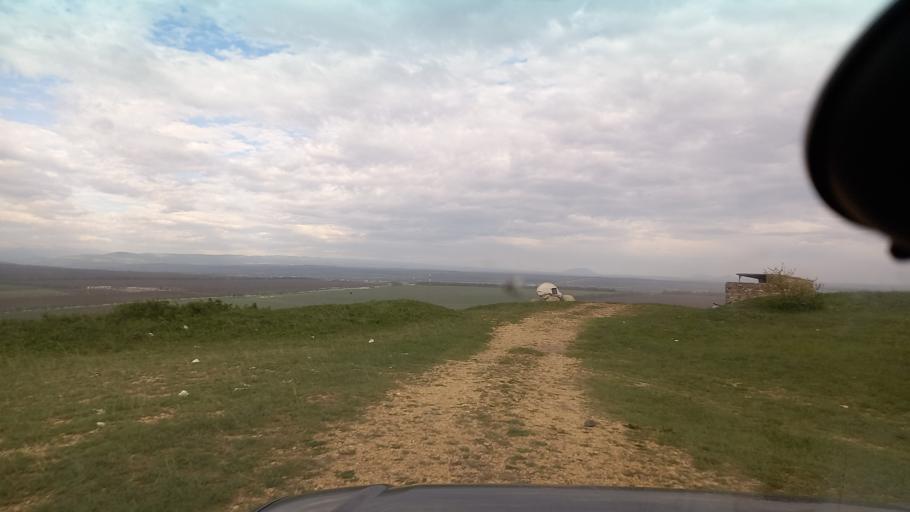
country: RU
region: Kabardino-Balkariya
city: Kuba-Taba
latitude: 43.8050
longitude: 43.4012
